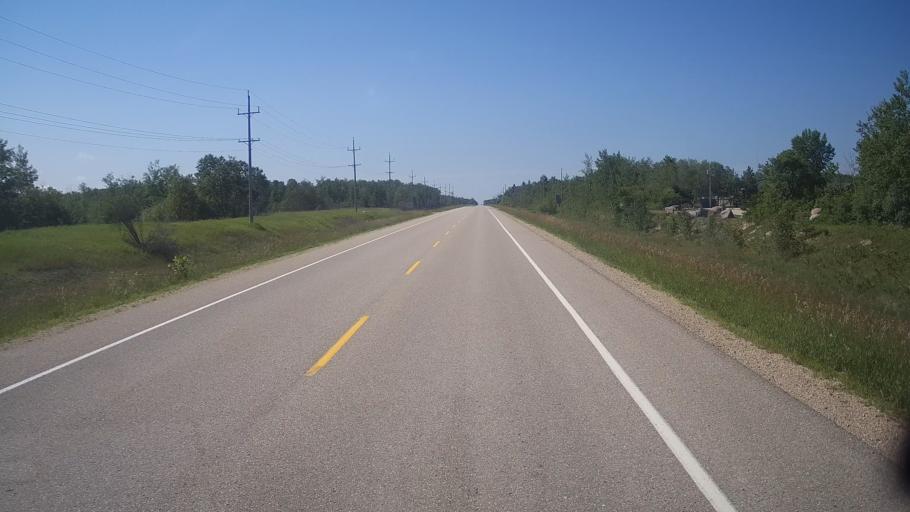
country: CA
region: Manitoba
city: La Broquerie
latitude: 49.6768
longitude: -96.4569
